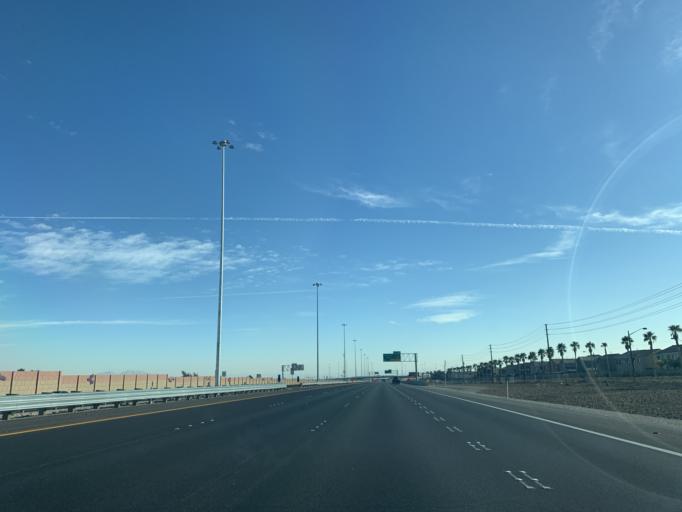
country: US
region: Nevada
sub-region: Clark County
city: Summerlin South
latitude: 36.3060
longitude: -115.2933
